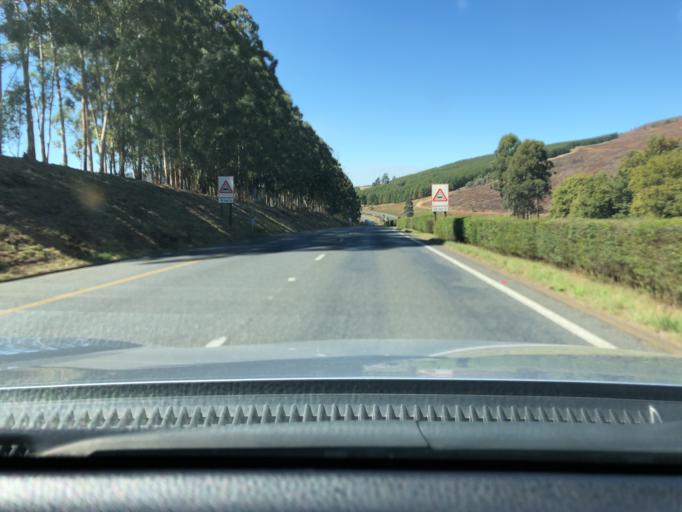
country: ZA
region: KwaZulu-Natal
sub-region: uMgungundlovu District Municipality
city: Howick
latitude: -29.3644
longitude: 30.1049
